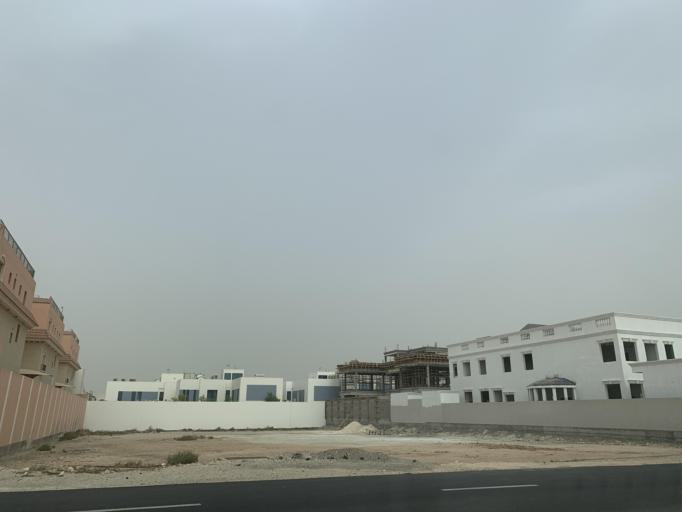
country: BH
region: Central Governorate
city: Madinat Hamad
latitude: 26.1403
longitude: 50.5244
